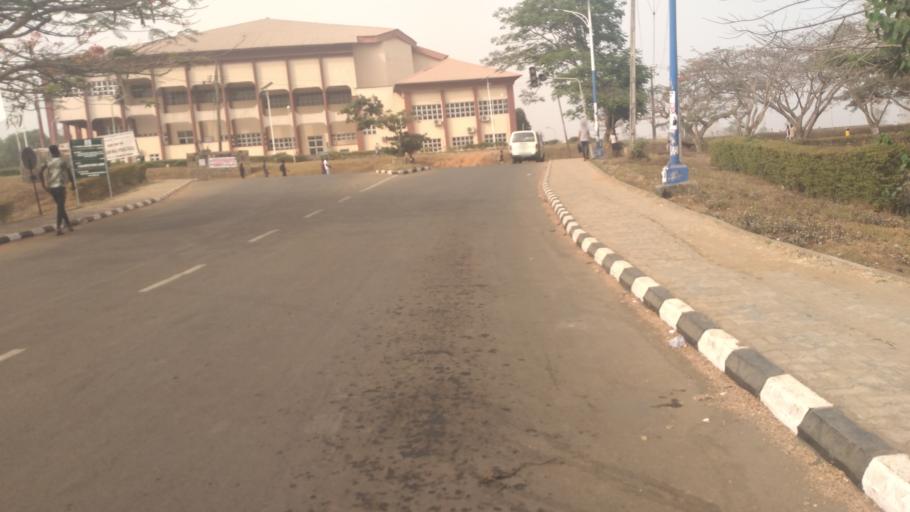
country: NG
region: Ondo
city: Ilare
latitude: 7.3032
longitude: 5.1368
